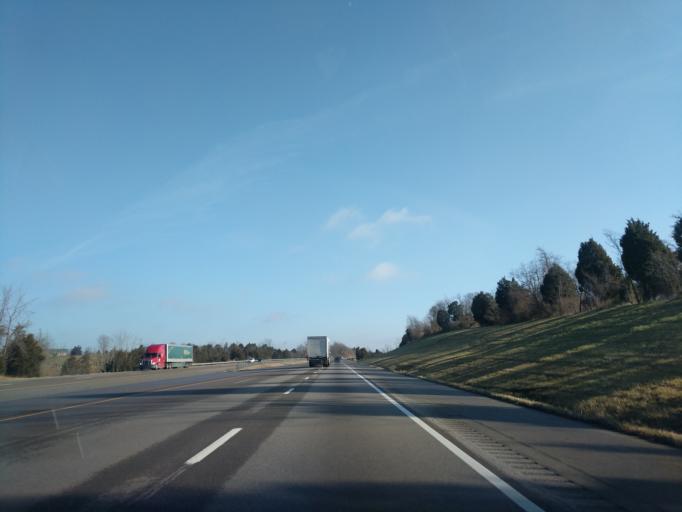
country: US
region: Kentucky
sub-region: Gallatin County
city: Warsaw
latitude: 38.7252
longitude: -84.8612
